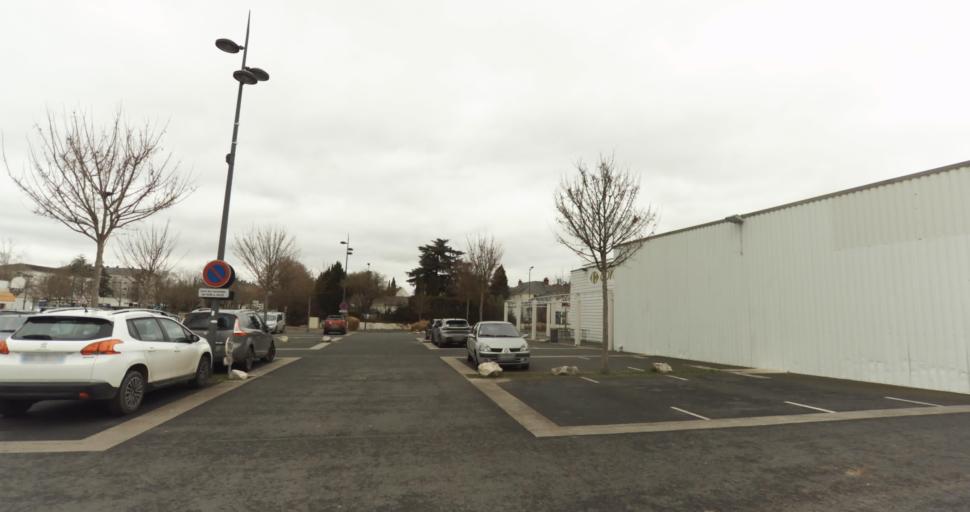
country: FR
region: Pays de la Loire
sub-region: Departement de Maine-et-Loire
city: Saumur
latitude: 47.2464
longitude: -0.0769
